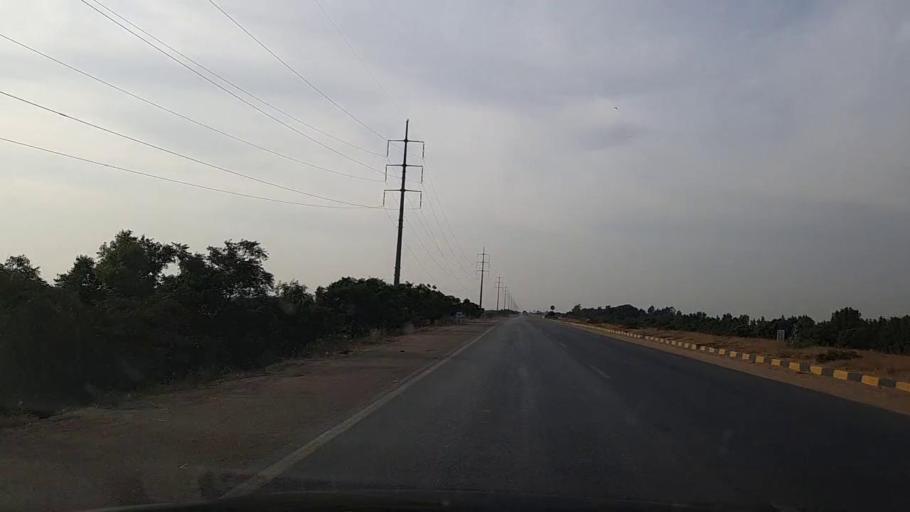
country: PK
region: Sindh
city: Gharo
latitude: 24.8221
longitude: 67.4807
